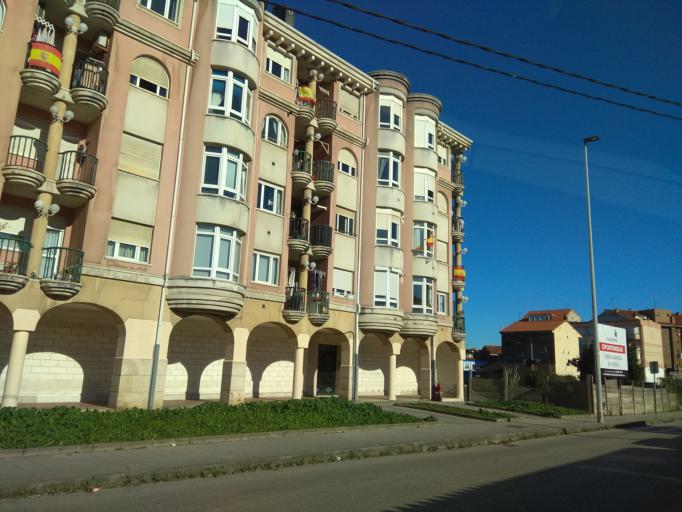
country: ES
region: Cantabria
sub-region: Provincia de Cantabria
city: Santander
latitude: 43.4626
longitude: -3.8416
